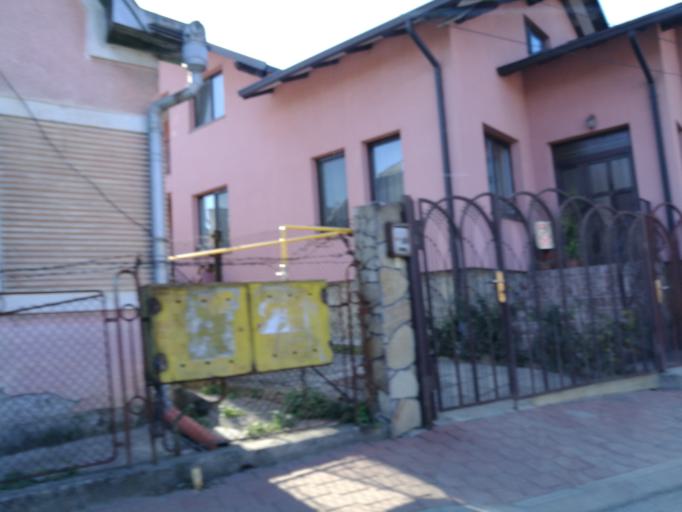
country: RO
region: Suceava
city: Suceava
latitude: 47.6509
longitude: 26.2544
